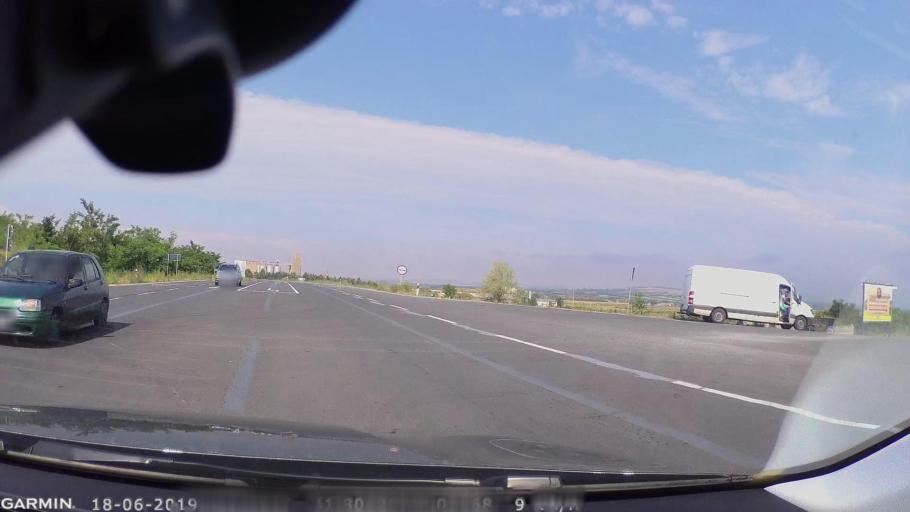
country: MK
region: Sveti Nikole
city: Sveti Nikole
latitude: 41.8242
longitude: 22.0104
